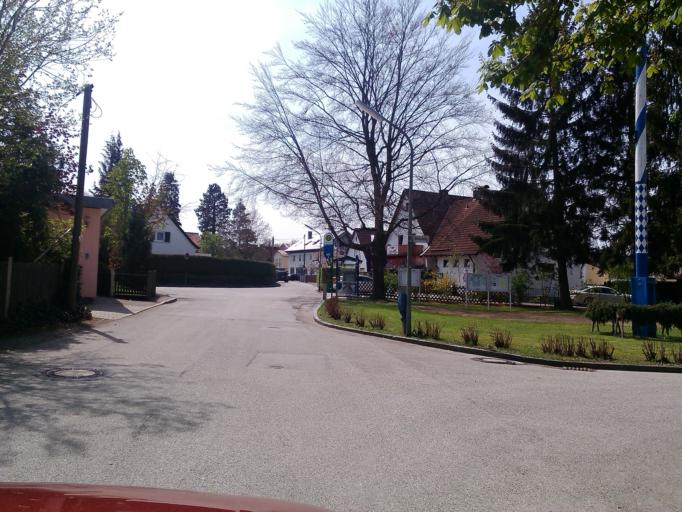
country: DE
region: Bavaria
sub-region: Upper Bavaria
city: Gauting
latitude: 48.0764
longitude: 11.3502
